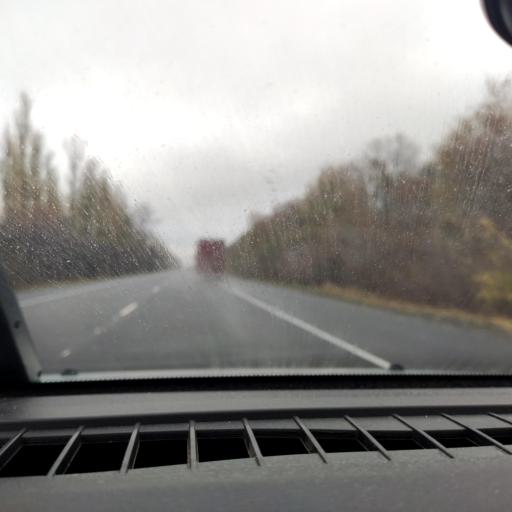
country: RU
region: Voronezj
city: Kolodeznyy
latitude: 51.2462
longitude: 39.0556
